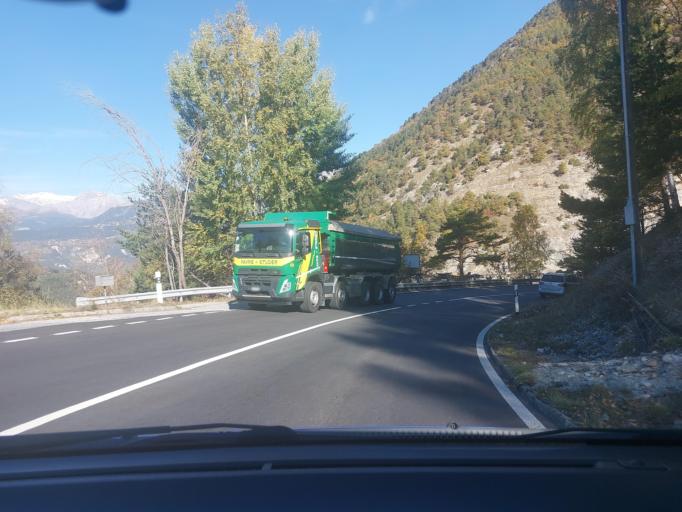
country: CH
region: Valais
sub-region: Sierre District
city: Chippis
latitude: 46.2603
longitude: 7.5639
